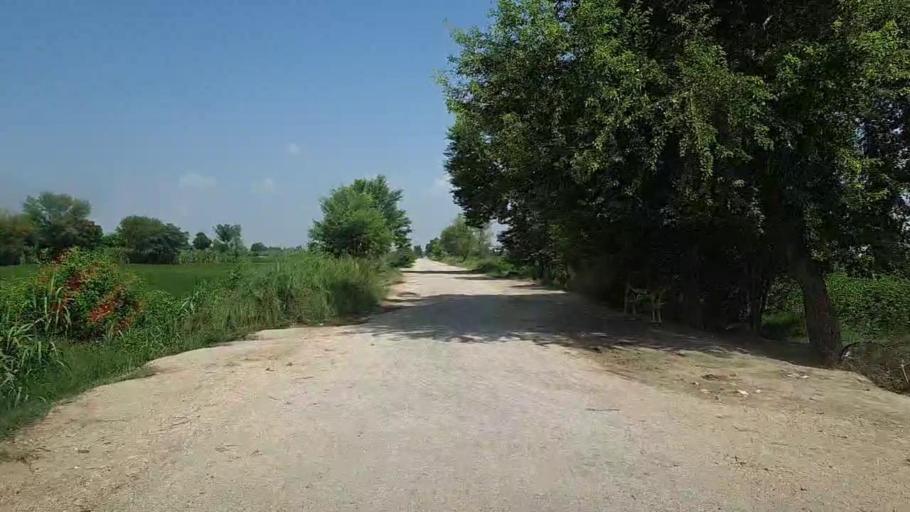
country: PK
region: Sindh
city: Bhiria
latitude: 26.8750
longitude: 68.2492
